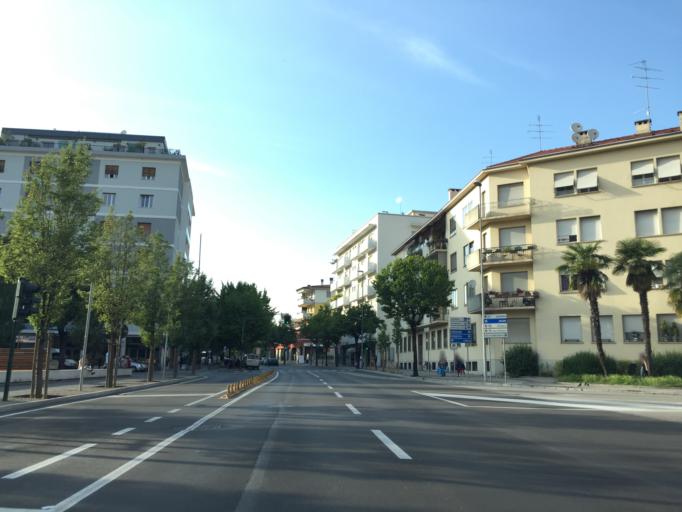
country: IT
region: Friuli Venezia Giulia
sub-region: Provincia di Pordenone
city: Pordenone
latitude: 45.9592
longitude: 12.6643
